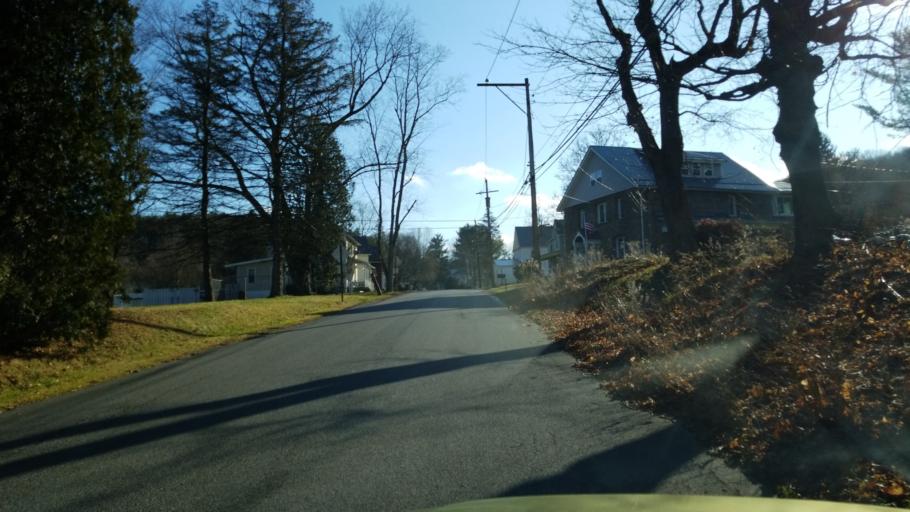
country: US
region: Pennsylvania
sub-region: Clearfield County
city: Clearfield
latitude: 41.0192
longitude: -78.4319
